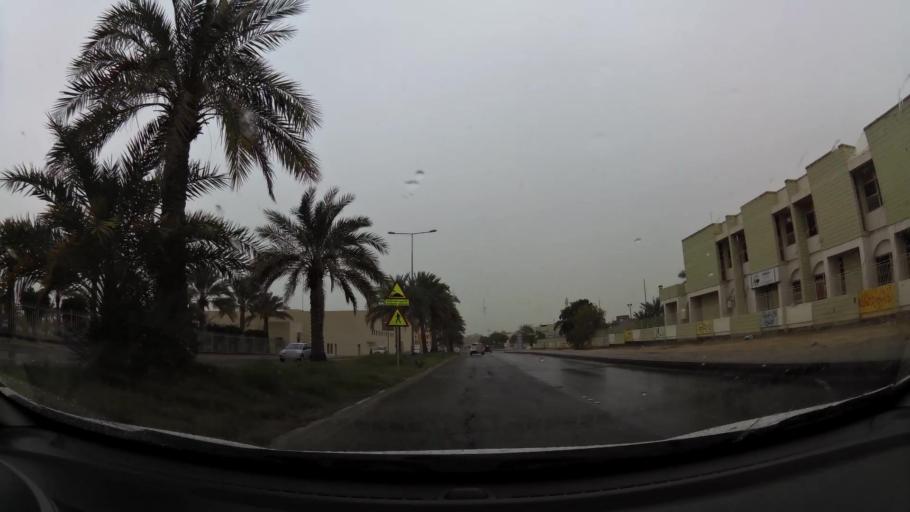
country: BH
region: Northern
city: Madinat `Isa
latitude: 26.1747
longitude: 50.5503
